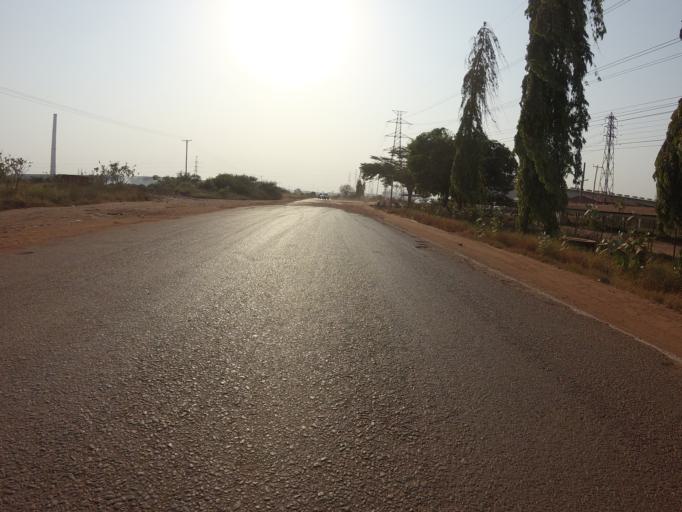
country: GH
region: Greater Accra
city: Tema
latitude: 5.6738
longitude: 0.0270
